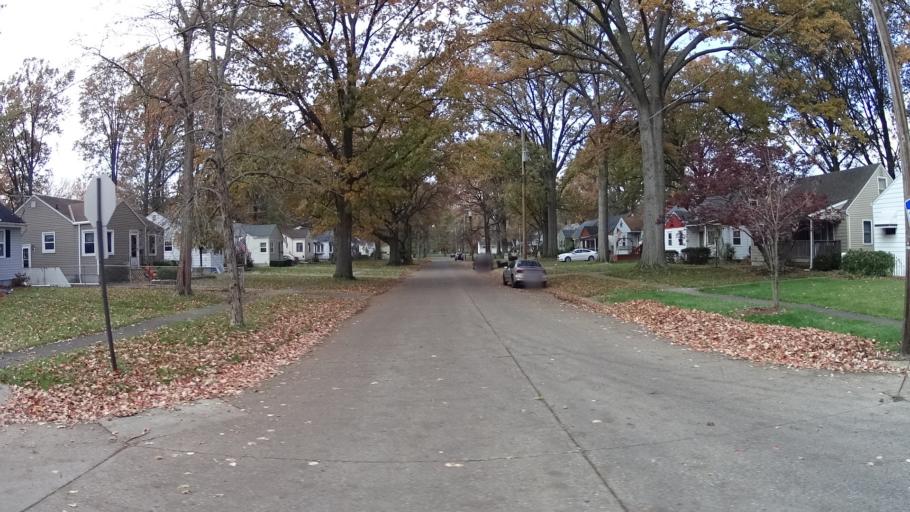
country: US
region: Ohio
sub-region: Lorain County
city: Elyria
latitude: 41.3613
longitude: -82.0861
